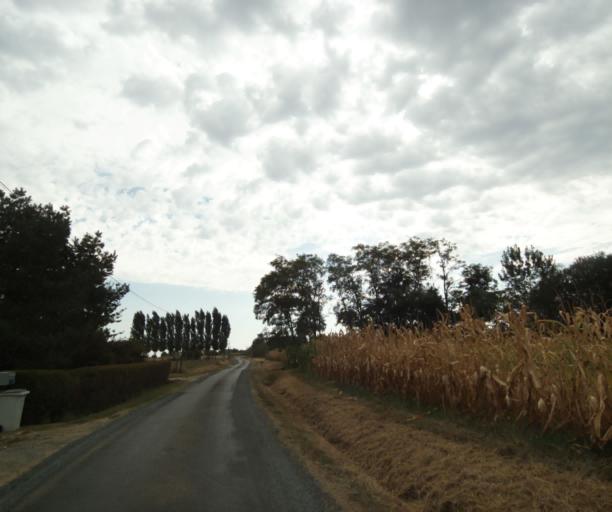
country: FR
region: Poitou-Charentes
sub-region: Departement de la Charente-Maritime
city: Tonnay-Charente
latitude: 45.9617
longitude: -0.8757
